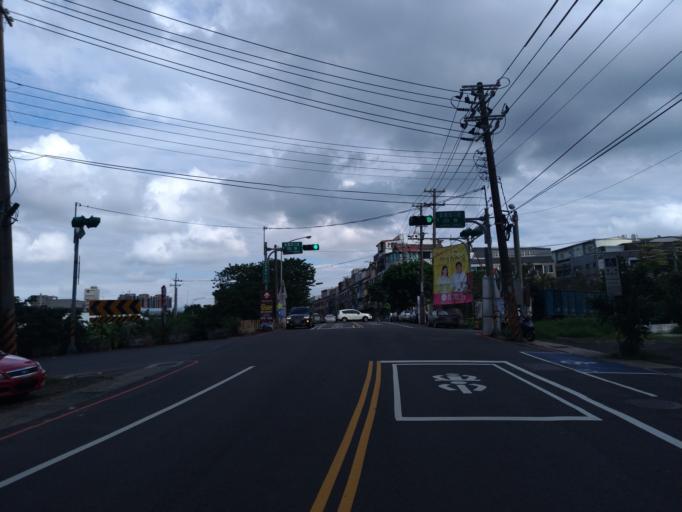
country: TW
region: Taiwan
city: Daxi
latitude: 24.9123
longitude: 121.1717
